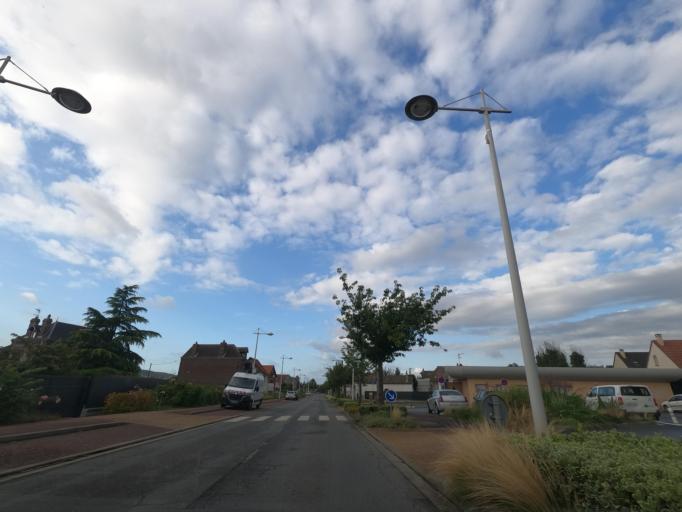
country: FR
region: Haute-Normandie
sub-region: Departement de la Seine-Maritime
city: Grand-Couronne
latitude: 49.3622
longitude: 1.0127
